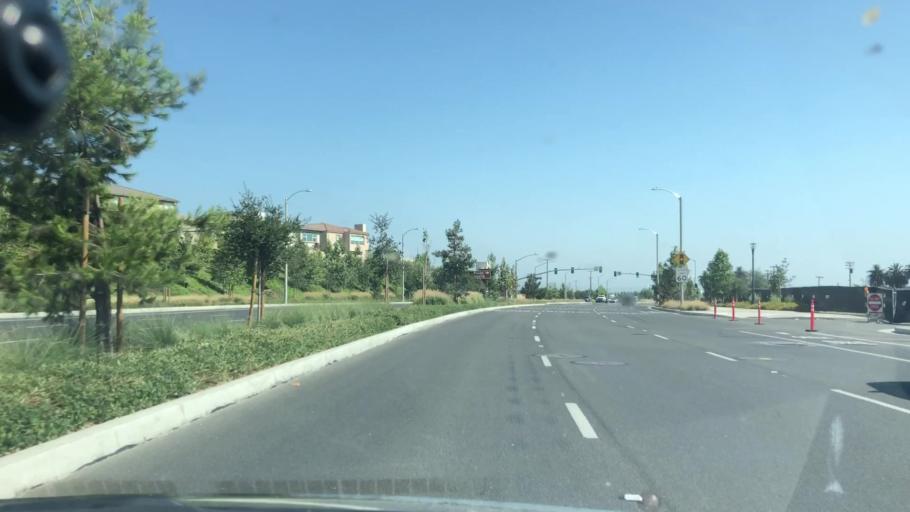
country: US
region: California
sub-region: Orange County
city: Lake Forest
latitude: 33.6820
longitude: -117.7160
